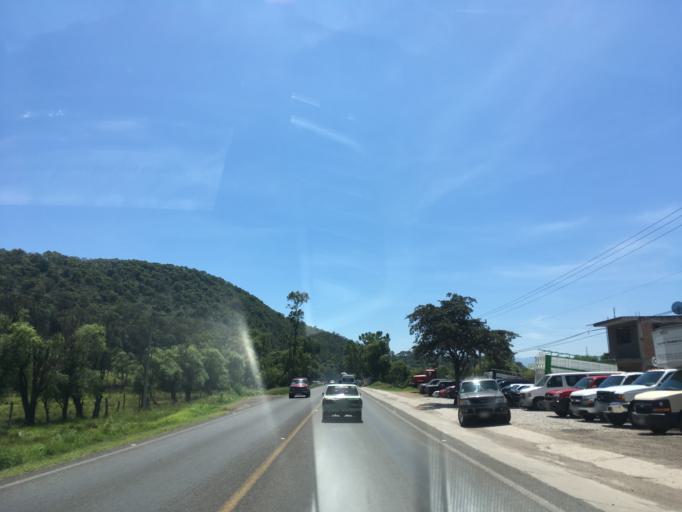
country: MX
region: Michoacan
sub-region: Hidalgo
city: Colonia Ecologica Asociacion de Lucha Social (Lucha Social)
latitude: 19.6991
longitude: -100.5961
